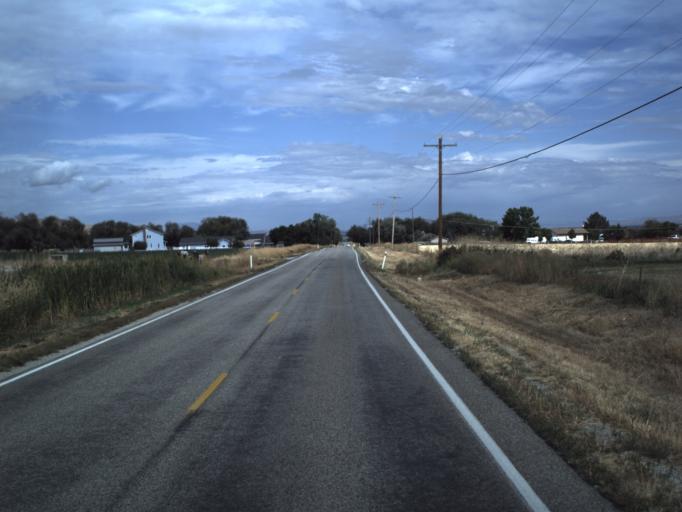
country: US
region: Utah
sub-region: Cache County
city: Mendon
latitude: 41.7262
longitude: -111.9791
